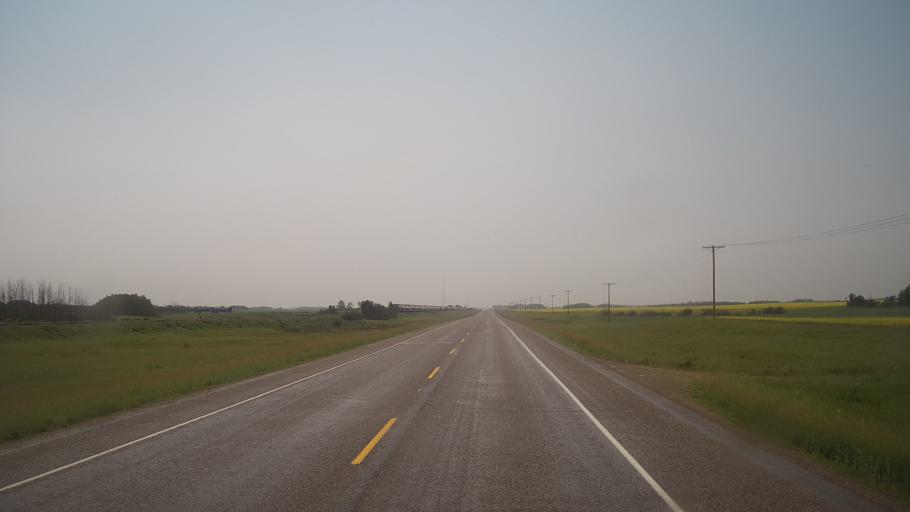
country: CA
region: Saskatchewan
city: Biggar
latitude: 52.1643
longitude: -108.2956
